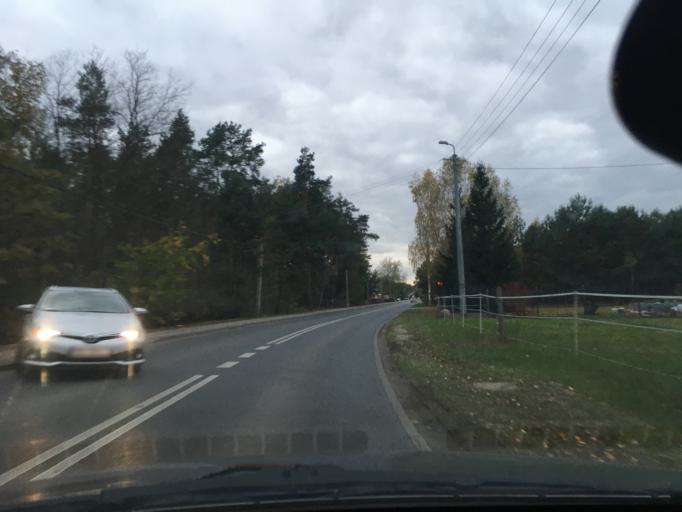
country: PL
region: Masovian Voivodeship
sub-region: Powiat piaseczynski
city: Lesznowola
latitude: 52.0667
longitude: 20.9331
